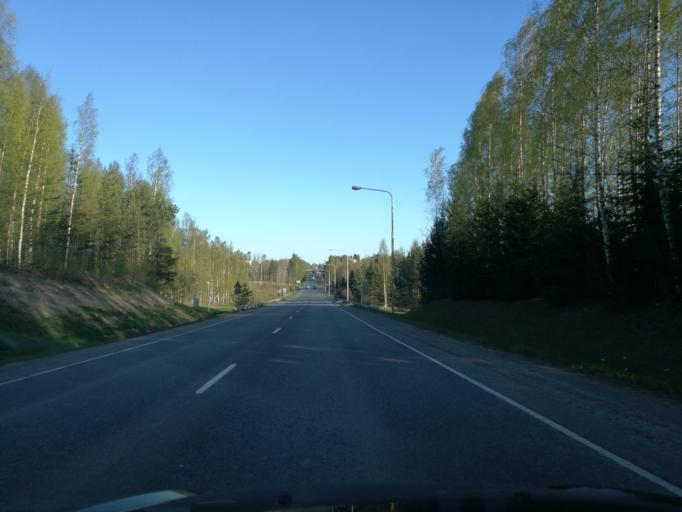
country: FI
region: Uusimaa
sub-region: Helsinki
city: Tuusula
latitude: 60.4027
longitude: 25.0104
